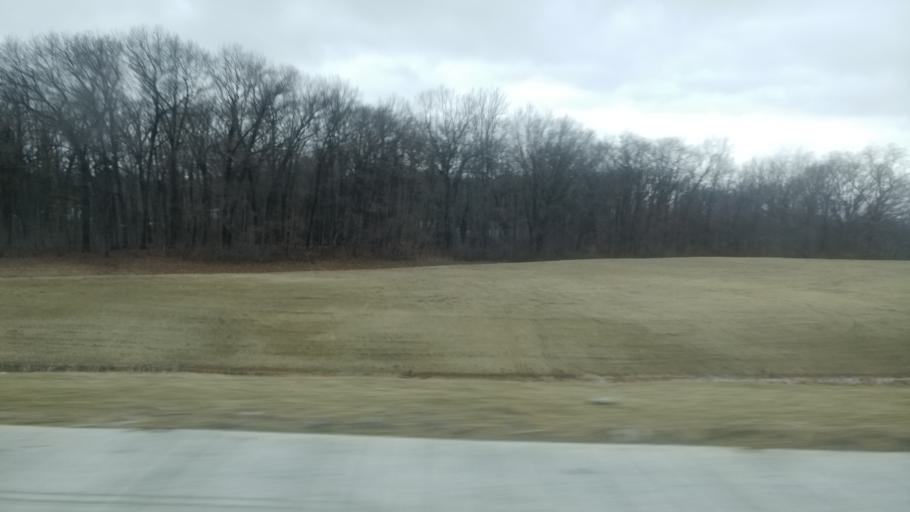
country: US
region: Ohio
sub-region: Lucas County
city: Sylvania
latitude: 41.6741
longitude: -83.6947
